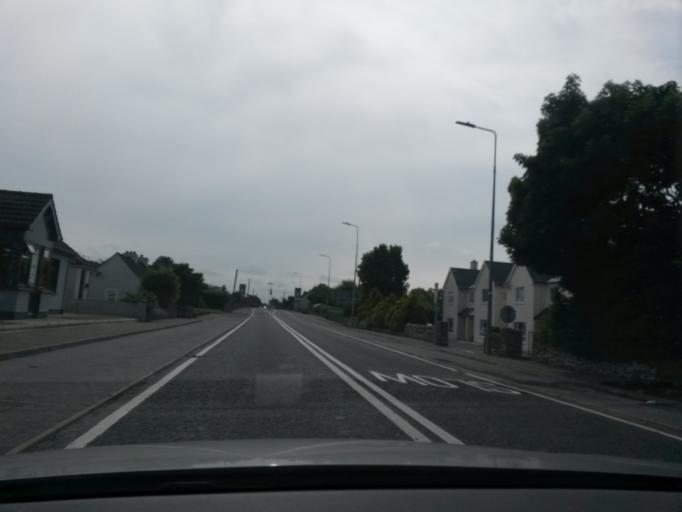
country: IE
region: Connaught
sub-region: Sligo
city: Sligo
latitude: 54.4298
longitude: -8.4549
